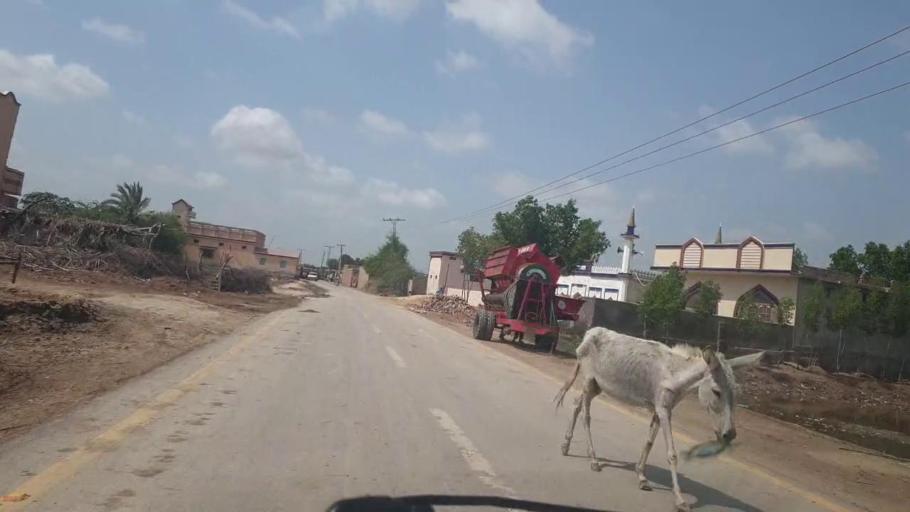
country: PK
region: Sindh
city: Berani
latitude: 25.6778
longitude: 68.9245
